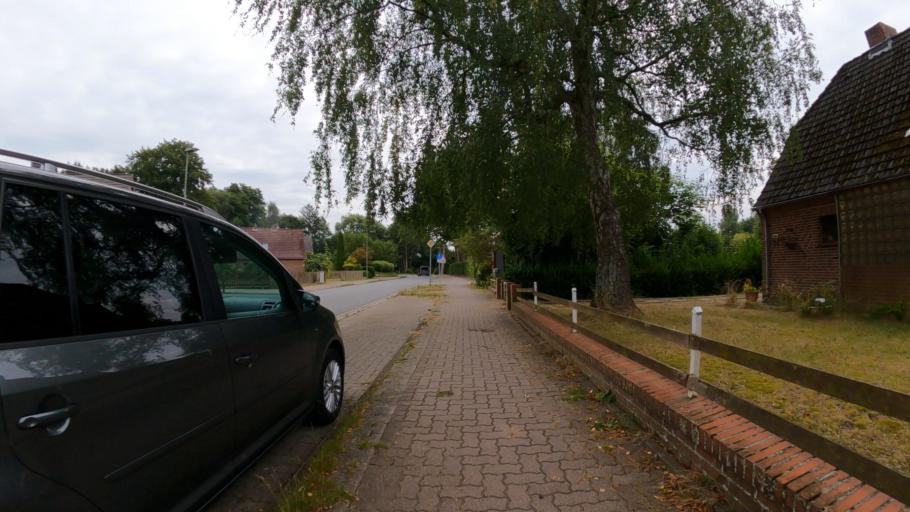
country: DE
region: Schleswig-Holstein
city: Boostedt
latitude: 54.0492
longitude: 10.0409
